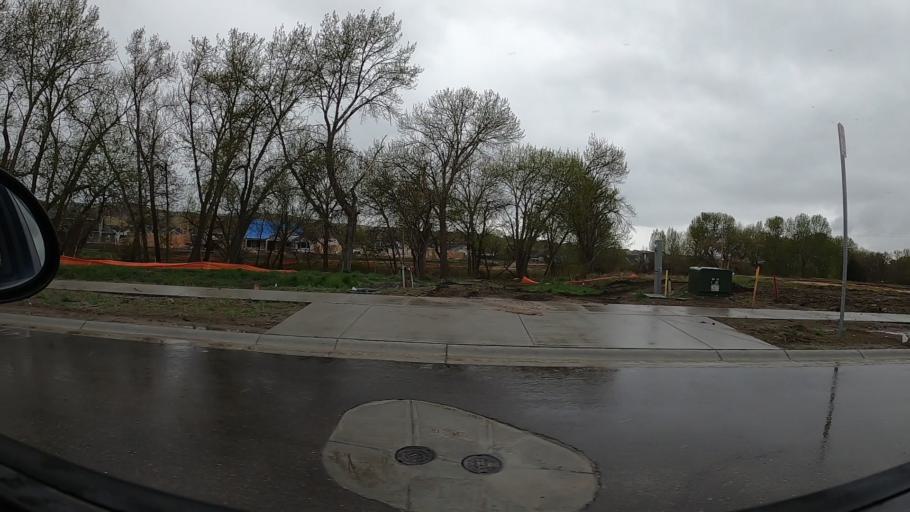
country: US
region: Idaho
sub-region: Ada County
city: Garden City
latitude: 43.7140
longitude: -116.2355
